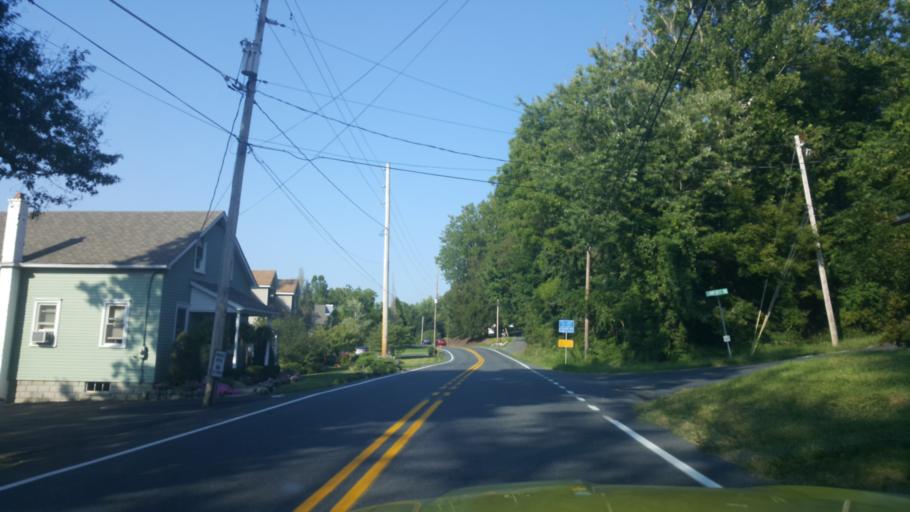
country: US
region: Pennsylvania
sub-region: Lebanon County
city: Campbelltown
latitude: 40.2216
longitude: -76.5382
